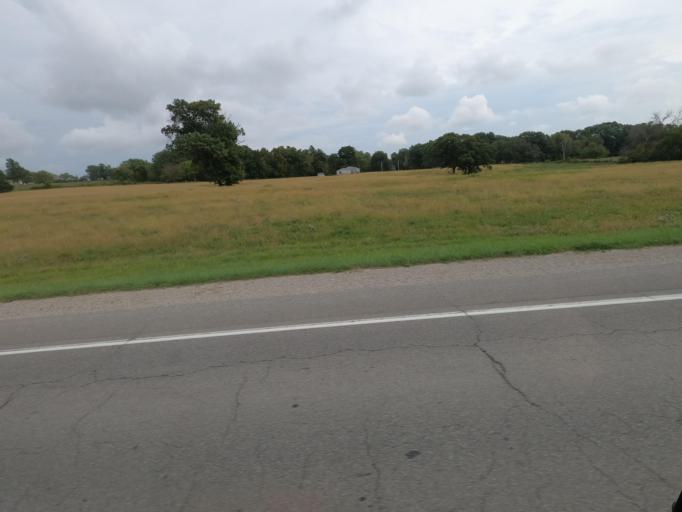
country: US
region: Iowa
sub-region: Wapello County
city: Ottumwa
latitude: 40.9262
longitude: -92.2294
